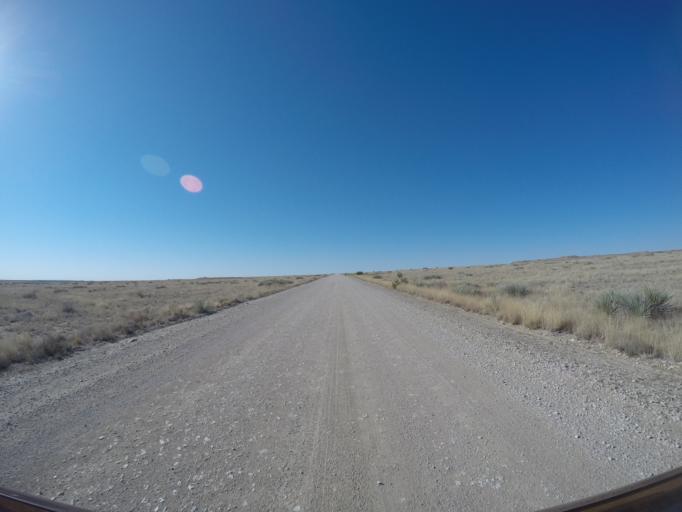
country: US
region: Colorado
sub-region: Otero County
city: La Junta
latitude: 37.8003
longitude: -103.5026
